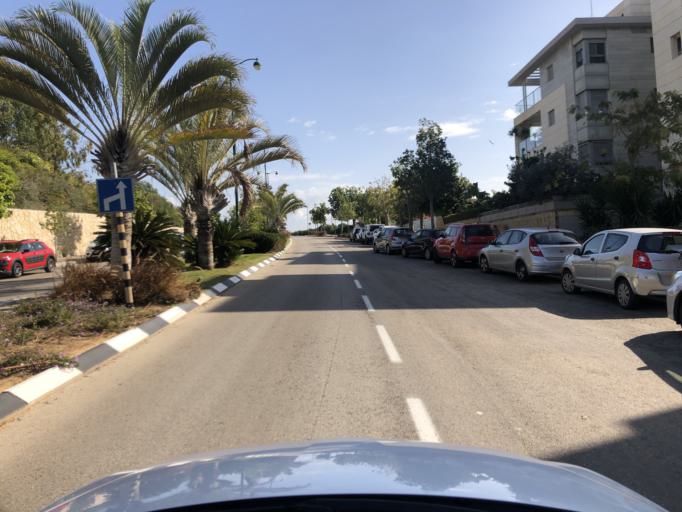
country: IL
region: Central District
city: Ness Ziona
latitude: 31.9142
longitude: 34.7917
